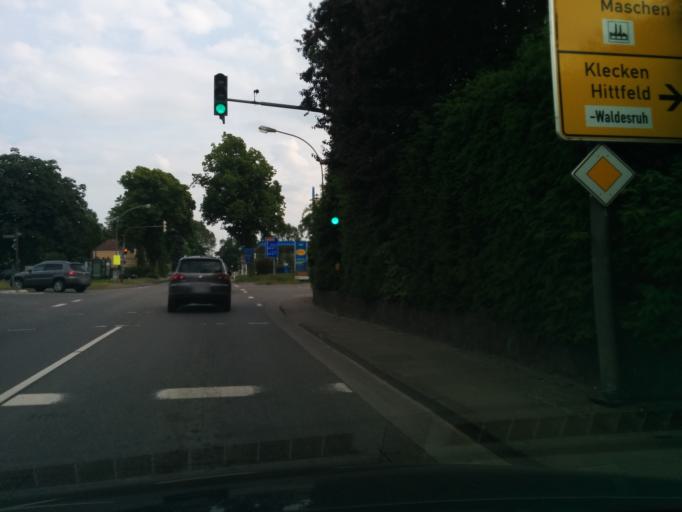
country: DE
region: Lower Saxony
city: Seevetal
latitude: 53.3834
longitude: 9.9791
